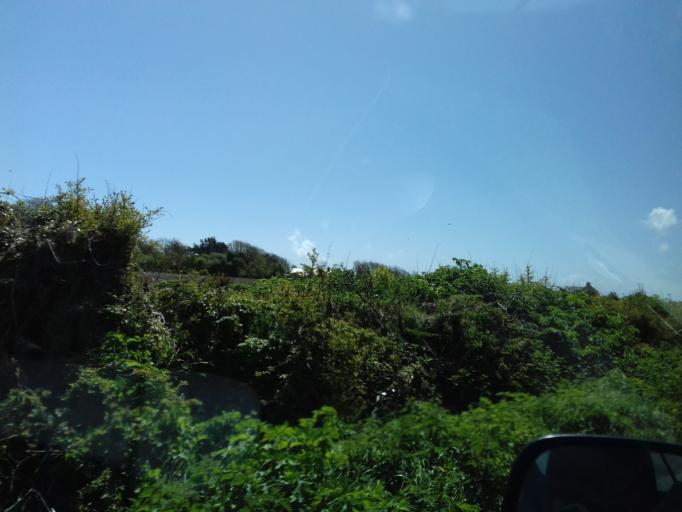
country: IE
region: Munster
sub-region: Waterford
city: Dunmore East
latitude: 52.1901
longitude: -6.8561
